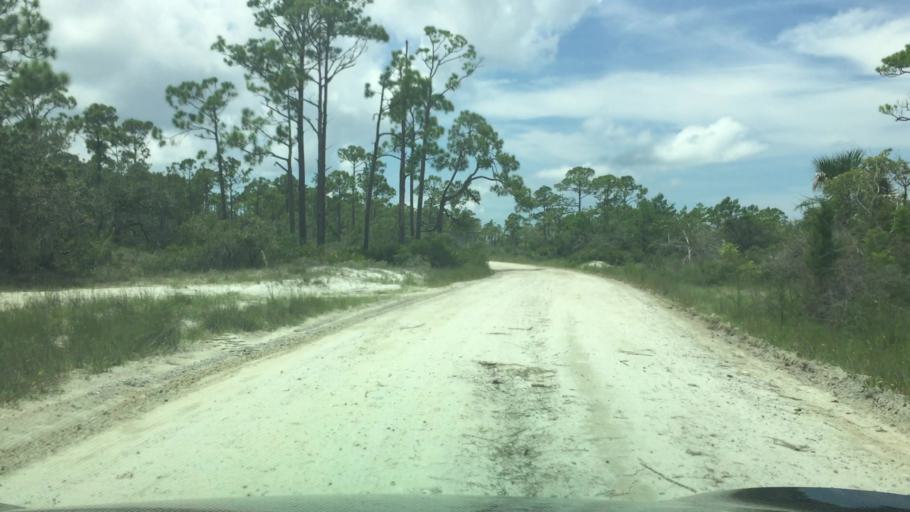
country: US
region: Florida
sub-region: Bay County
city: Mexico Beach
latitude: 29.9627
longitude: -85.4488
